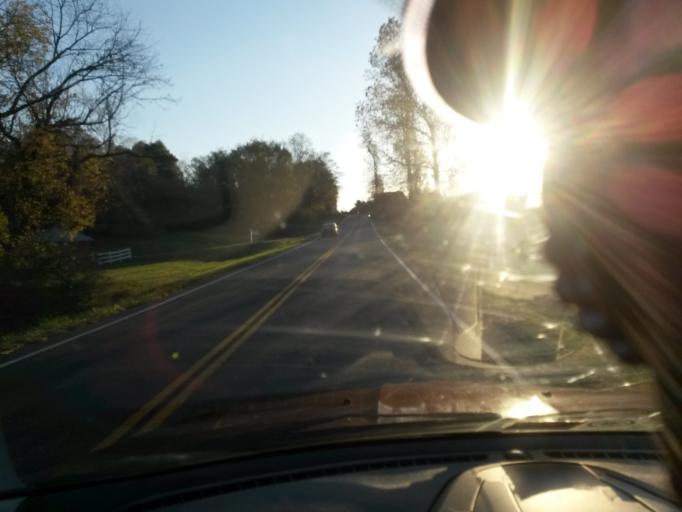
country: US
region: Virginia
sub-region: Franklin County
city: North Shore
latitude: 37.1281
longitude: -79.7587
